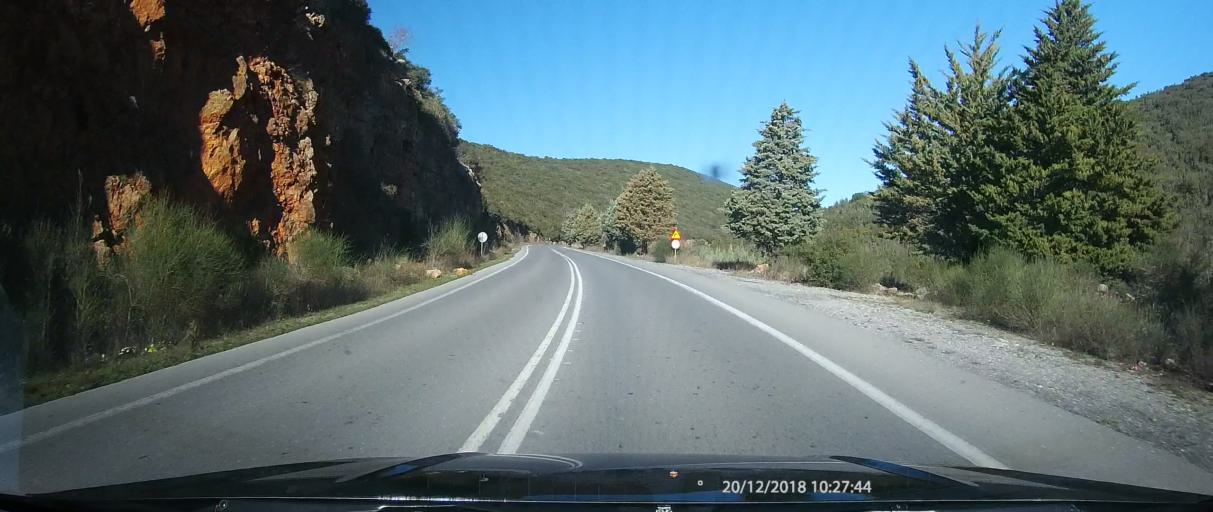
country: GR
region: Peloponnese
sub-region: Nomos Lakonias
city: Kariai
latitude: 37.2498
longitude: 22.4380
